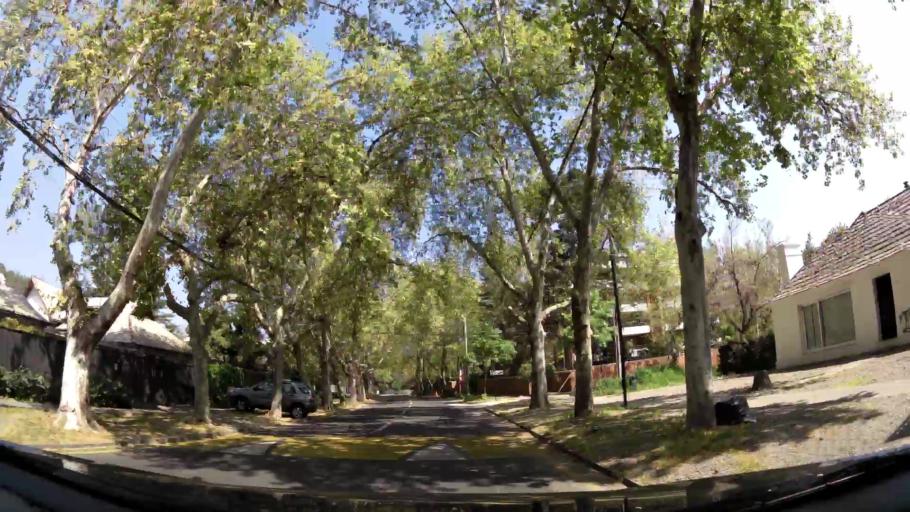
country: CL
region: Santiago Metropolitan
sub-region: Provincia de Santiago
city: Villa Presidente Frei, Nunoa, Santiago, Chile
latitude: -33.3959
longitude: -70.5920
